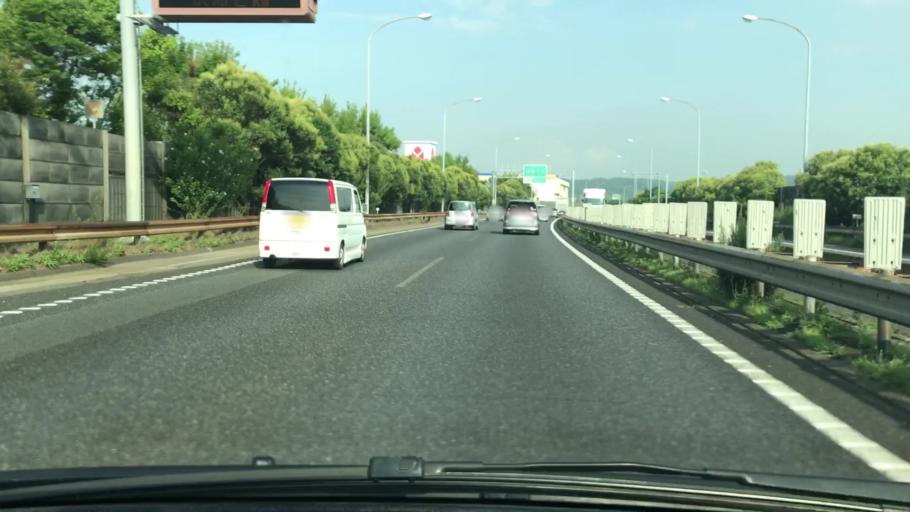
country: JP
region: Hyogo
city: Akashi
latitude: 34.6832
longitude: 134.9849
